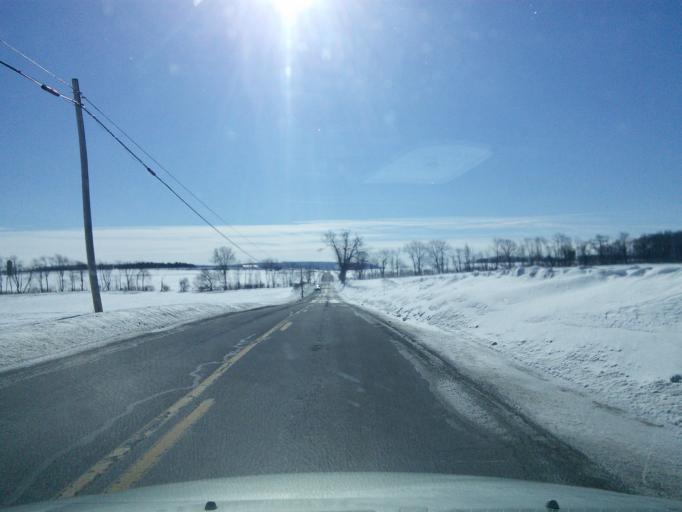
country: US
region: Pennsylvania
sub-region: Centre County
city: Houserville
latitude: 40.8717
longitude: -77.8447
